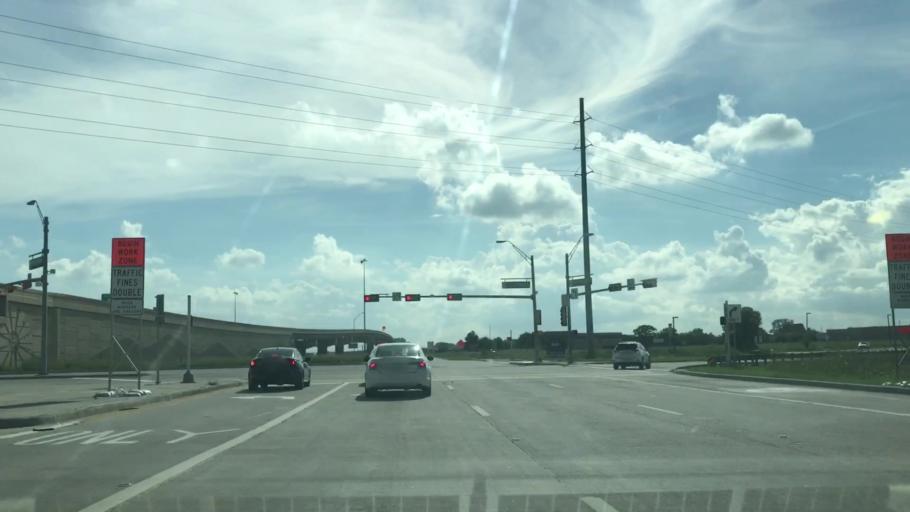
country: US
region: Texas
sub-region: Dallas County
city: Coppell
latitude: 32.9737
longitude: -97.0289
